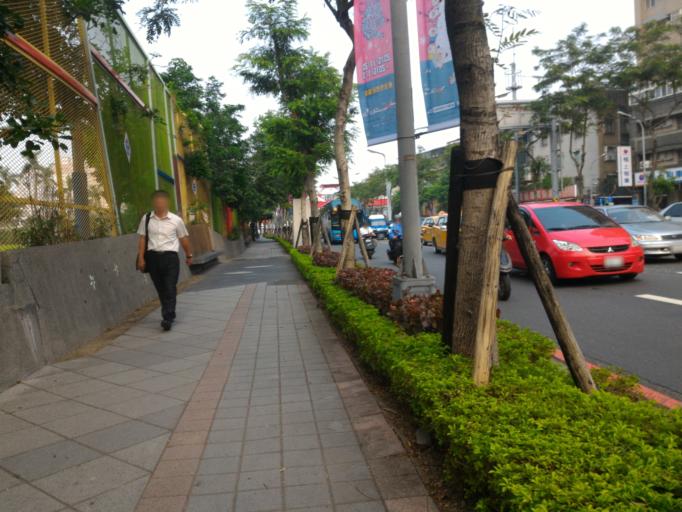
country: TW
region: Taipei
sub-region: Taipei
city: Banqiao
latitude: 25.0166
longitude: 121.4680
